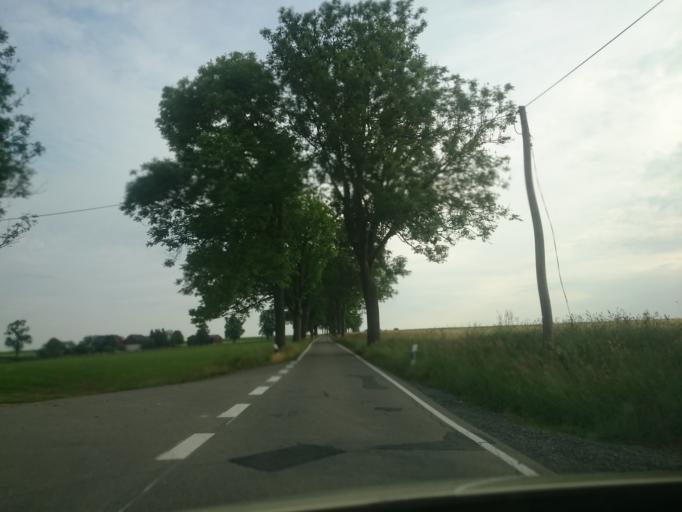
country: DE
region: Saxony
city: Eppendorf
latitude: 50.8446
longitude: 13.2343
